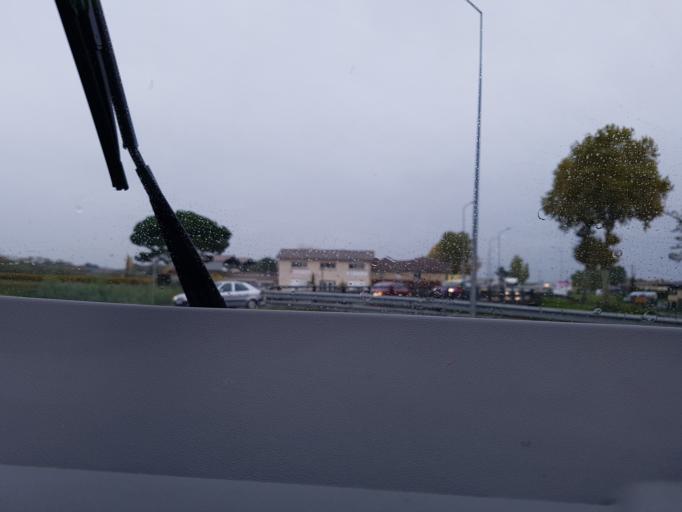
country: FR
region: Aquitaine
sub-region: Departement de la Gironde
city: Cubzac-les-Ponts
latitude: 44.9930
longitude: -0.4334
